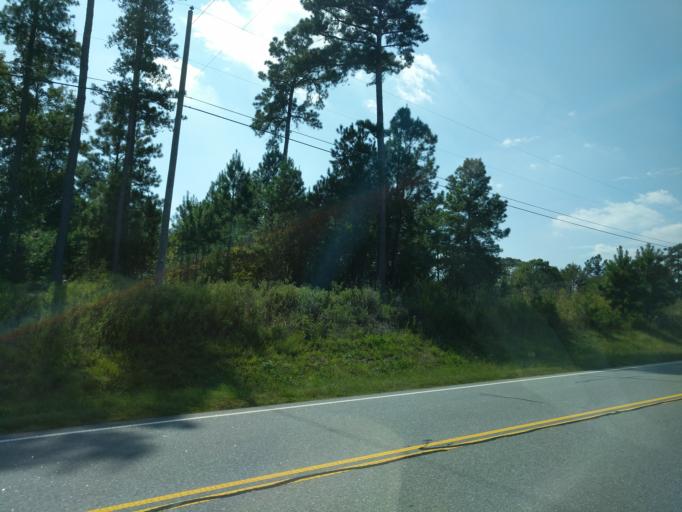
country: US
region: Georgia
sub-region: Hart County
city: Hartwell
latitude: 34.3688
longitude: -82.9837
